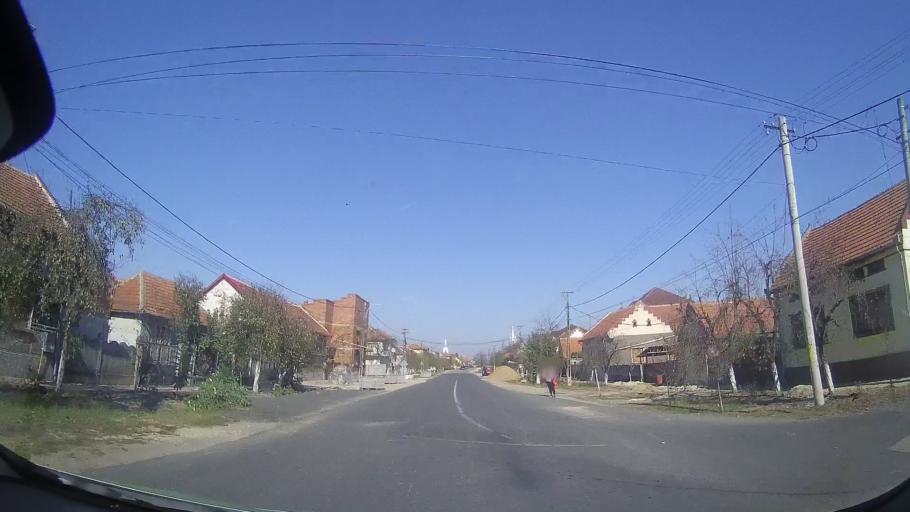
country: RO
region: Timis
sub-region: Comuna Costeiu
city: Costeiu
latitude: 45.7388
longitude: 21.8493
